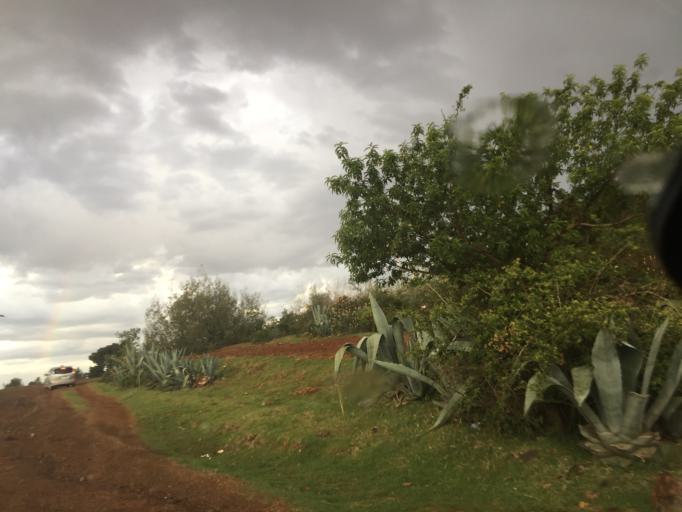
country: LS
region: Berea
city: Teyateyaneng
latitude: -29.1591
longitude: 28.0332
